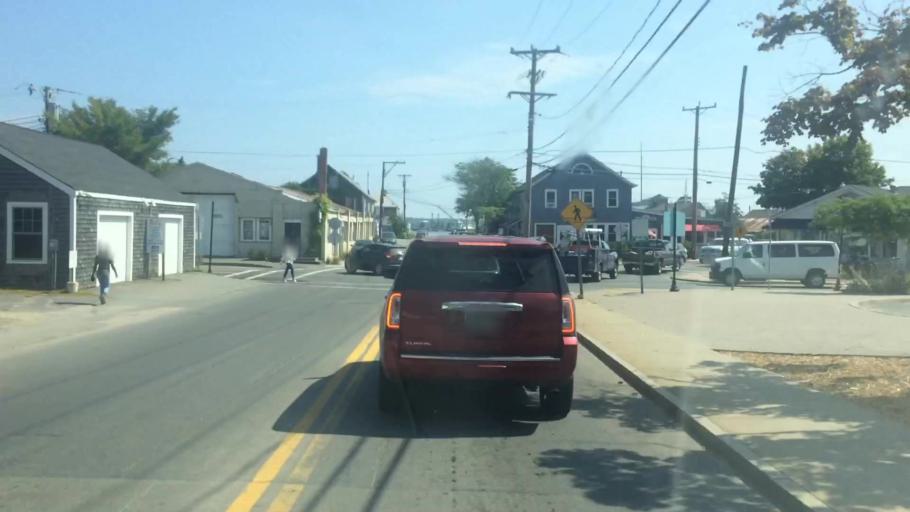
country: US
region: Massachusetts
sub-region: Dukes County
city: Vineyard Haven
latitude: 41.4535
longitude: -70.6023
